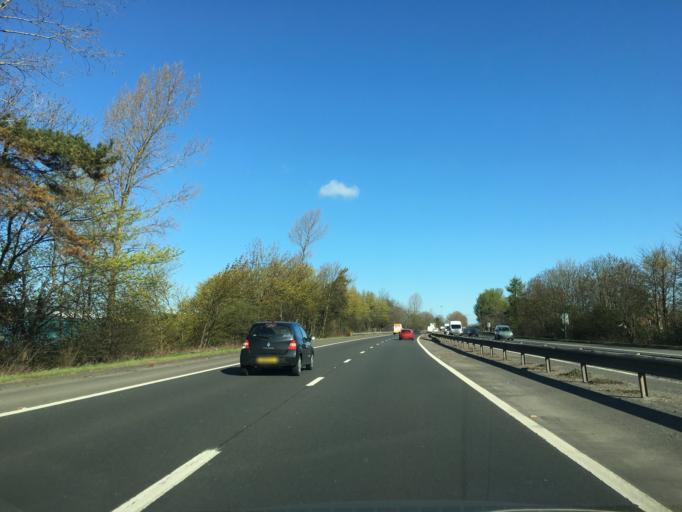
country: GB
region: Scotland
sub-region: Falkirk
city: Grangemouth
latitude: 56.0043
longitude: -3.7366
